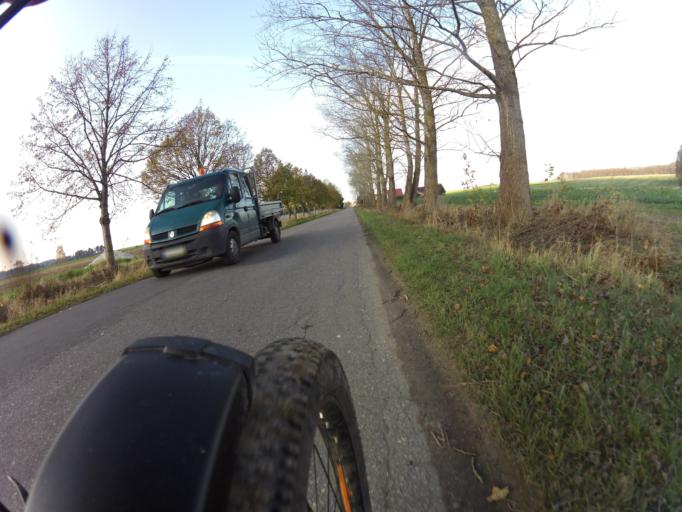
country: PL
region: Pomeranian Voivodeship
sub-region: Powiat pucki
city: Krokowa
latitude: 54.7558
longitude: 18.1845
